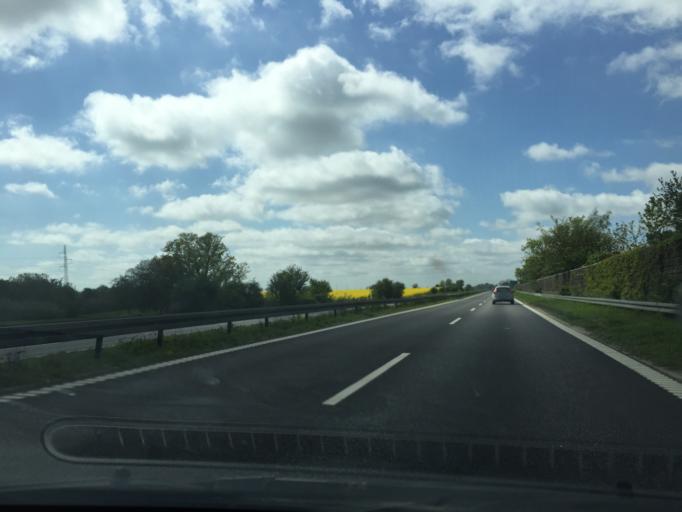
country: DK
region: Zealand
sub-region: Guldborgsund Kommune
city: Sakskobing
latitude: 54.7919
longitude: 11.6364
